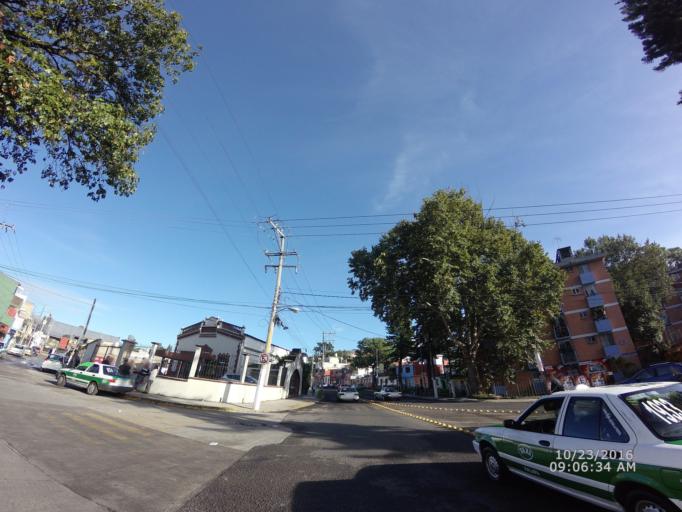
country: TR
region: Canakkale
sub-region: Goekceada
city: Gokceada
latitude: 40.2202
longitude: 26.0318
